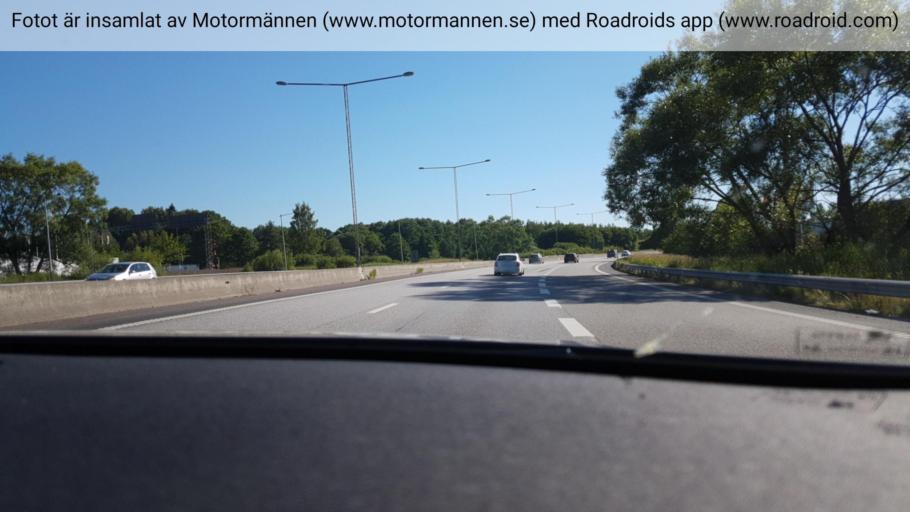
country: SE
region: Joenkoeping
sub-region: Jonkopings Kommun
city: Jonkoping
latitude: 57.7628
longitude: 14.1885
